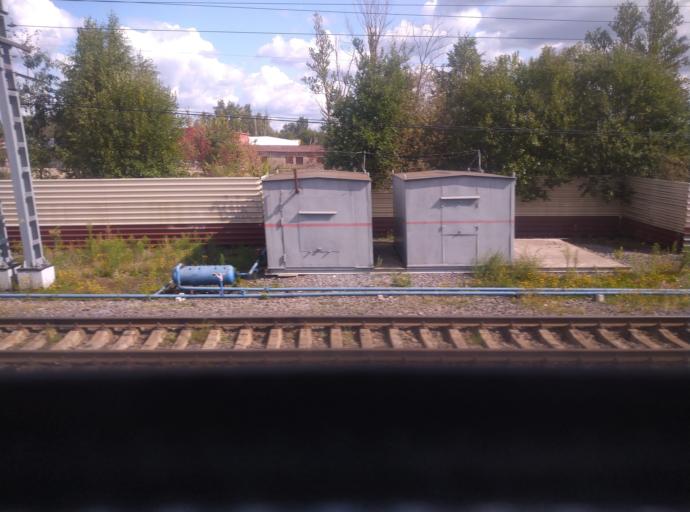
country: RU
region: St.-Petersburg
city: Kolpino
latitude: 59.7544
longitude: 30.6072
